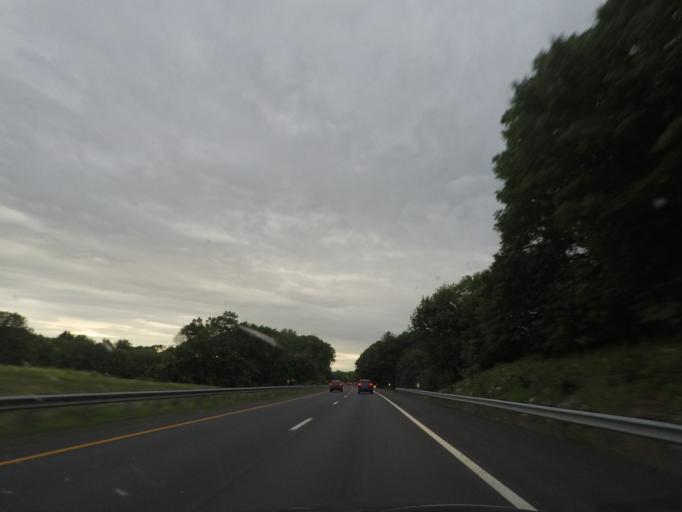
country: US
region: New York
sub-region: Rensselaer County
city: Nassau
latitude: 42.4786
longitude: -73.6203
